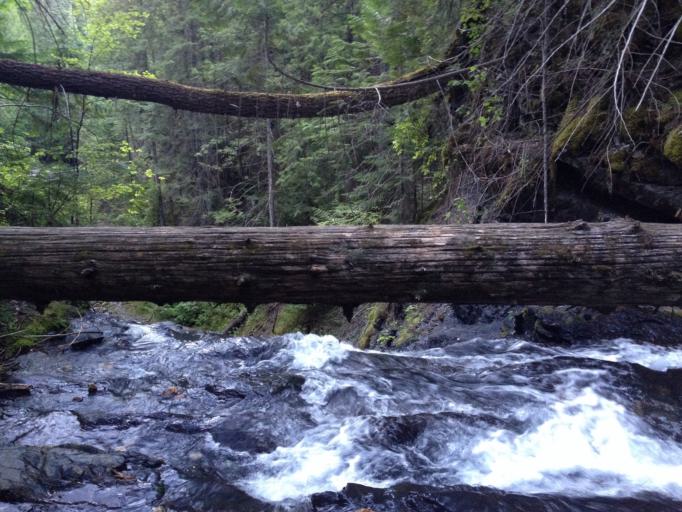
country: CA
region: British Columbia
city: Fruitvale
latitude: 48.8234
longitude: -117.3998
